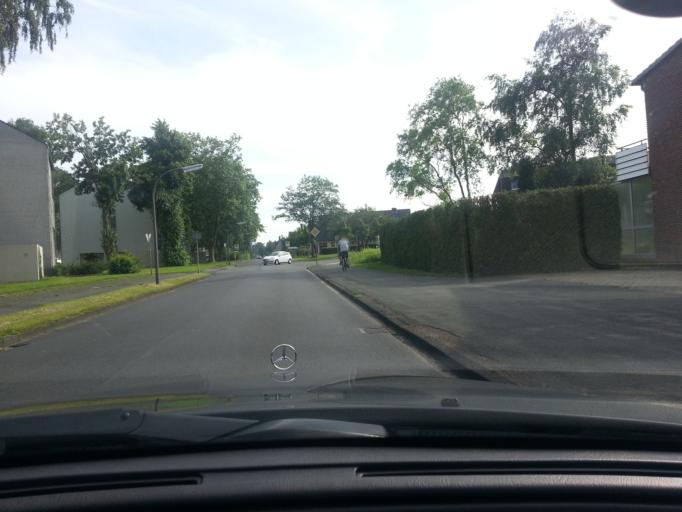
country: DE
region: North Rhine-Westphalia
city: Oer-Erkenschwick
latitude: 51.6391
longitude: 7.2482
